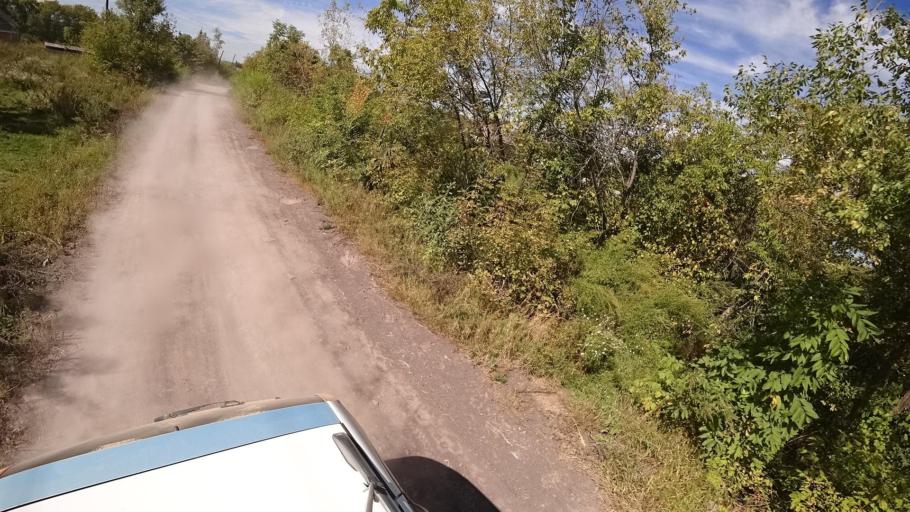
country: RU
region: Primorskiy
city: Yakovlevka
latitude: 44.4319
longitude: 133.5705
